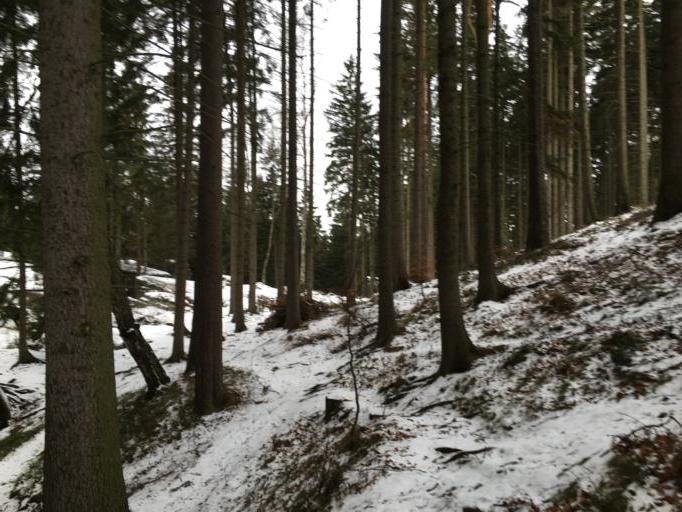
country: PL
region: Lower Silesian Voivodeship
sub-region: Powiat kamiennogorski
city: Krzeszow
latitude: 50.6957
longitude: 16.0999
